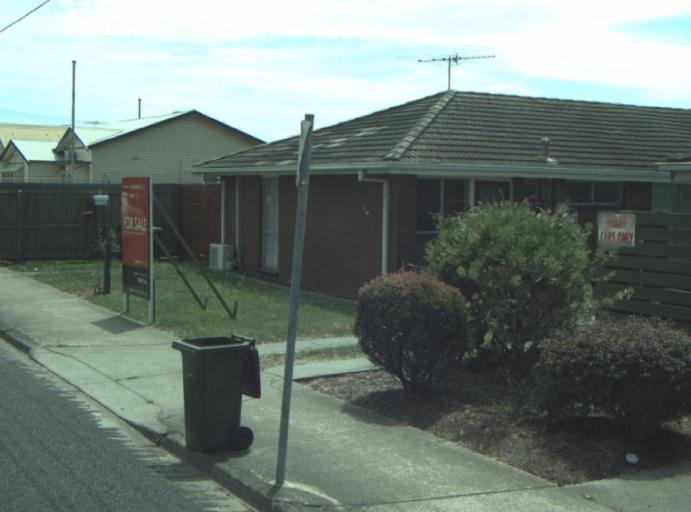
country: AU
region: Victoria
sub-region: Greater Geelong
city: Geelong West
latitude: -38.1344
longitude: 144.3455
